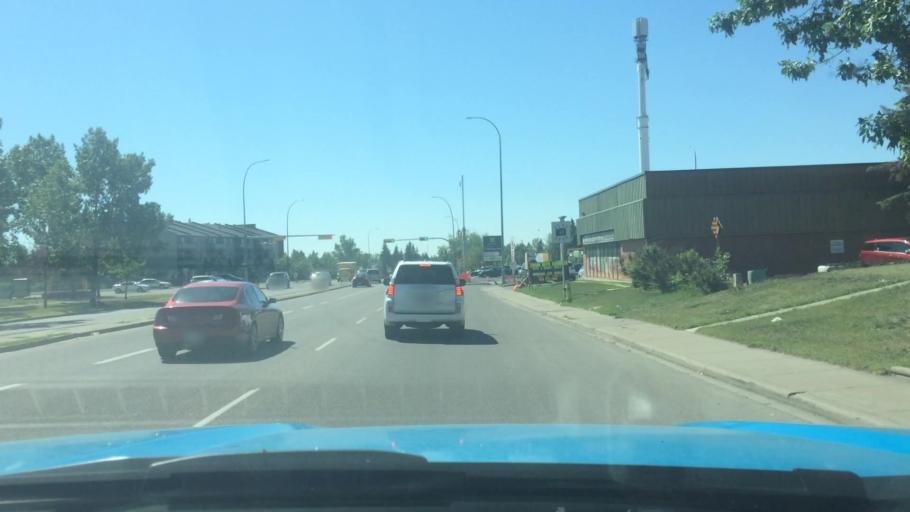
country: CA
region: Alberta
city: Calgary
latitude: 51.0543
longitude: -113.9564
